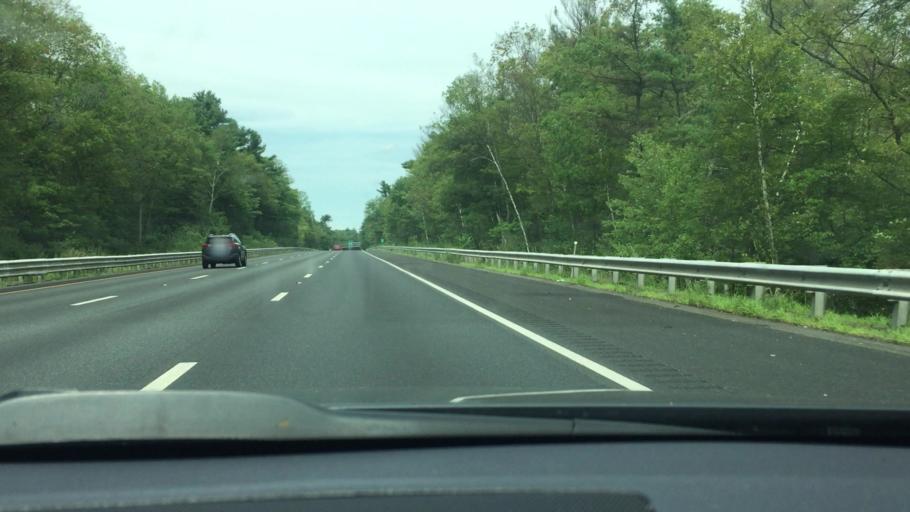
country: US
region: Massachusetts
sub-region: Norfolk County
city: Foxborough
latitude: 42.0994
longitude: -71.2269
